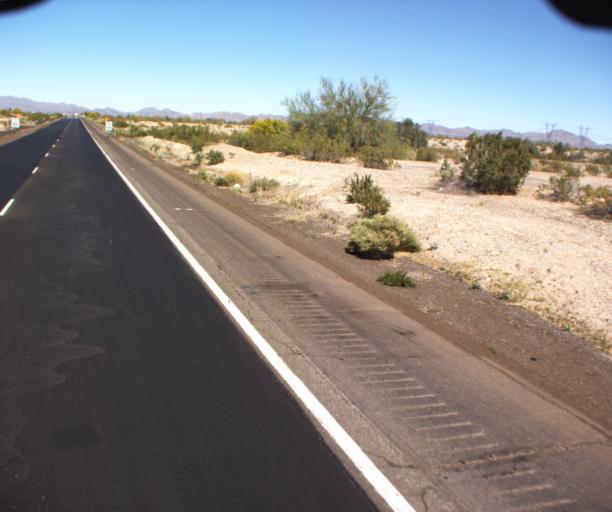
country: US
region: Arizona
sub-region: Maricopa County
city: Gila Bend
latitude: 32.9817
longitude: -112.6678
